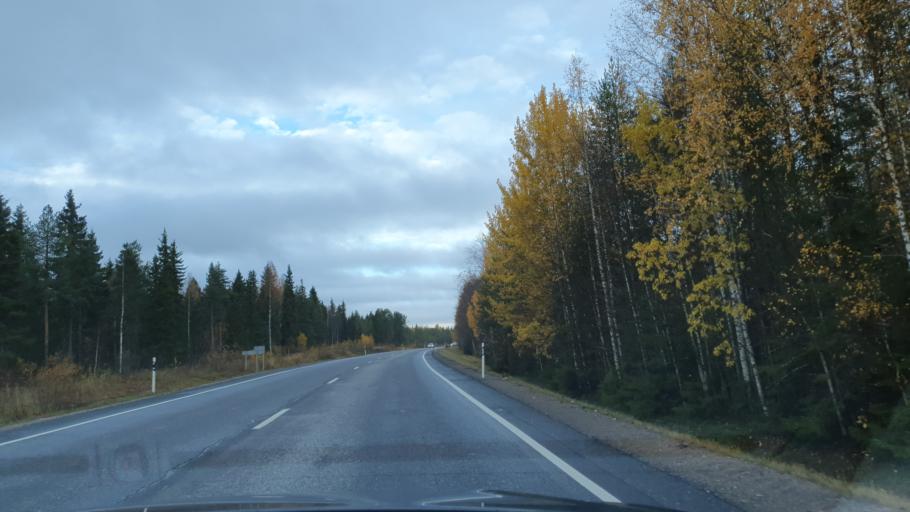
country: FI
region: Lapland
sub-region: Rovaniemi
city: Rovaniemi
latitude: 66.5795
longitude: 25.6232
